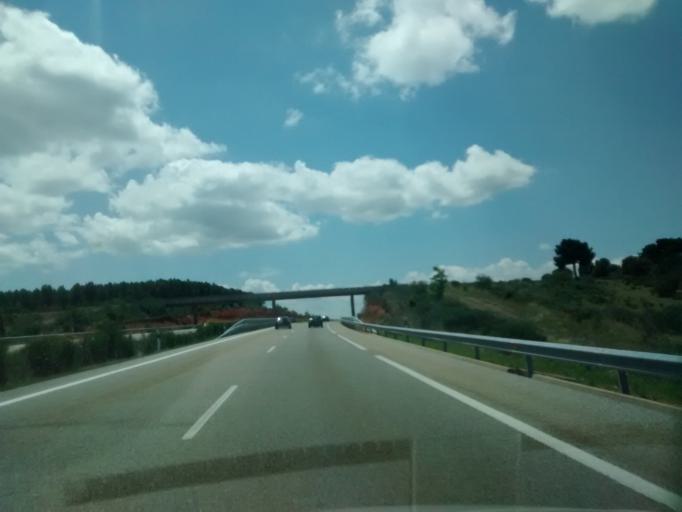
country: ES
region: Castille and Leon
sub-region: Provincia de Leon
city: Brazuelo
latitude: 42.5100
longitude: -6.1169
